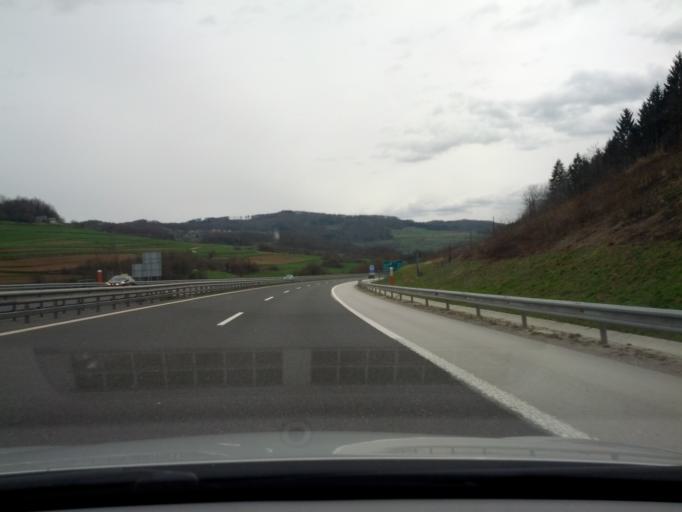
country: SI
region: Mirna Pec
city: Mirna Pec
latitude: 45.8736
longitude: 15.1052
